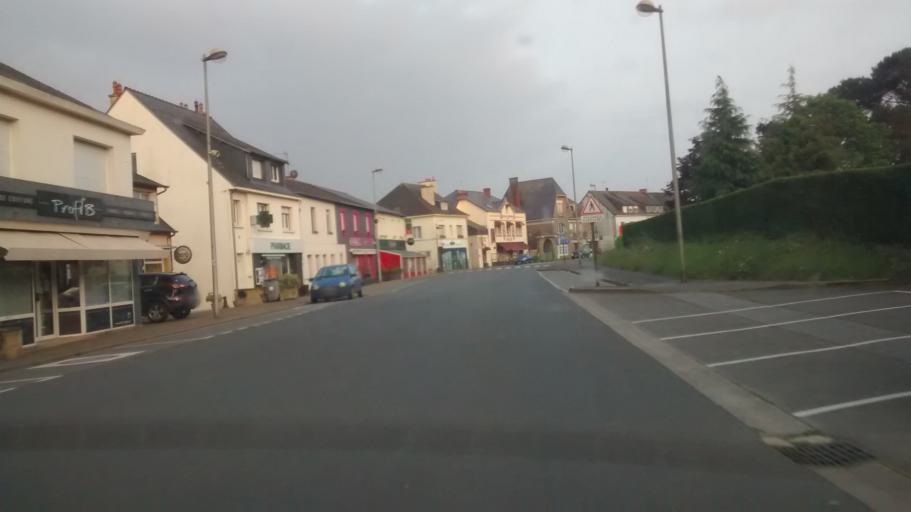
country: FR
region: Brittany
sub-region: Departement du Morbihan
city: Guer
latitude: 47.9449
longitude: -2.1318
